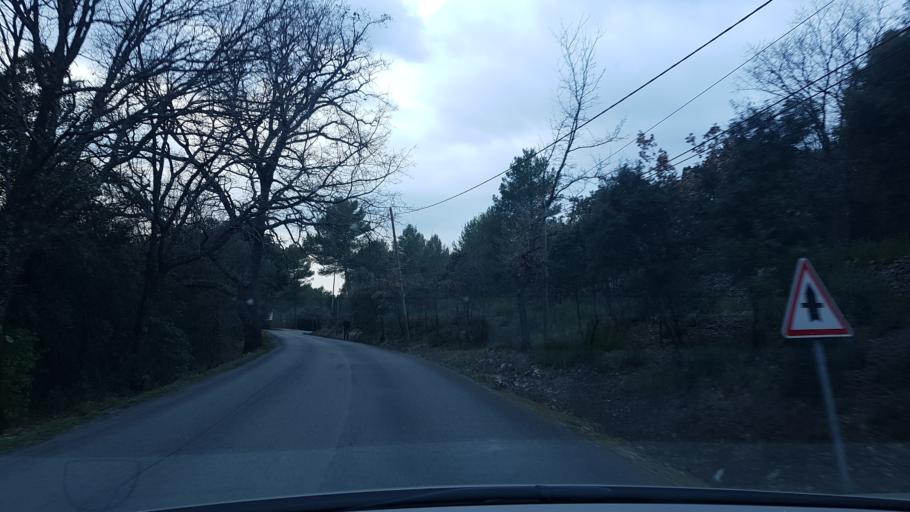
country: FR
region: Provence-Alpes-Cote d'Azur
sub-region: Departement des Bouches-du-Rhone
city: Mimet
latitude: 43.4351
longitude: 5.4995
